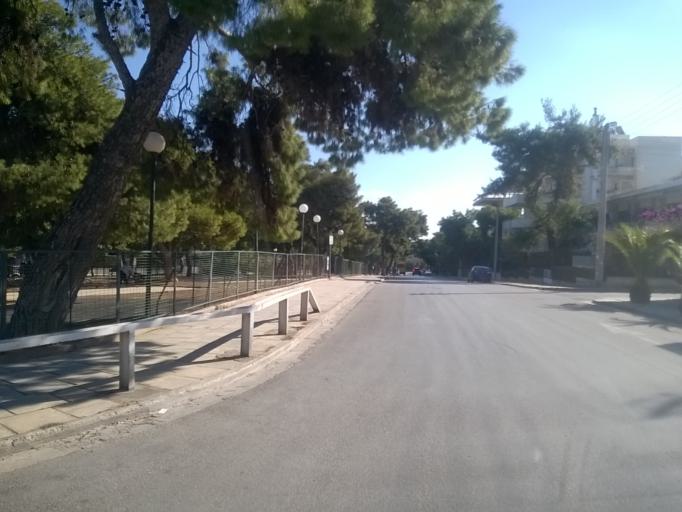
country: GR
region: Attica
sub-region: Nomarchia Anatolikis Attikis
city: Vari
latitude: 37.8168
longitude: 23.7971
